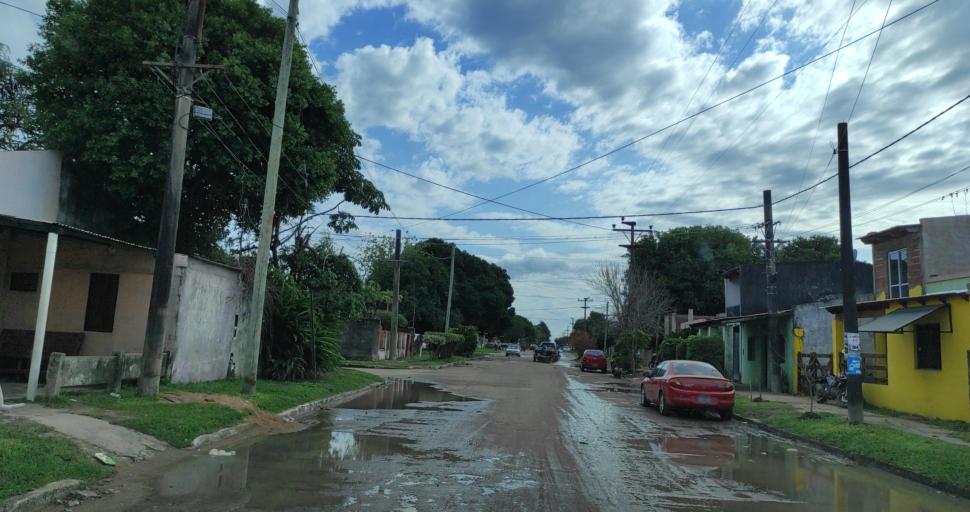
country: AR
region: Corrientes
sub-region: Departamento de Itati
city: Itati
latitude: -27.2747
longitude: -58.2405
